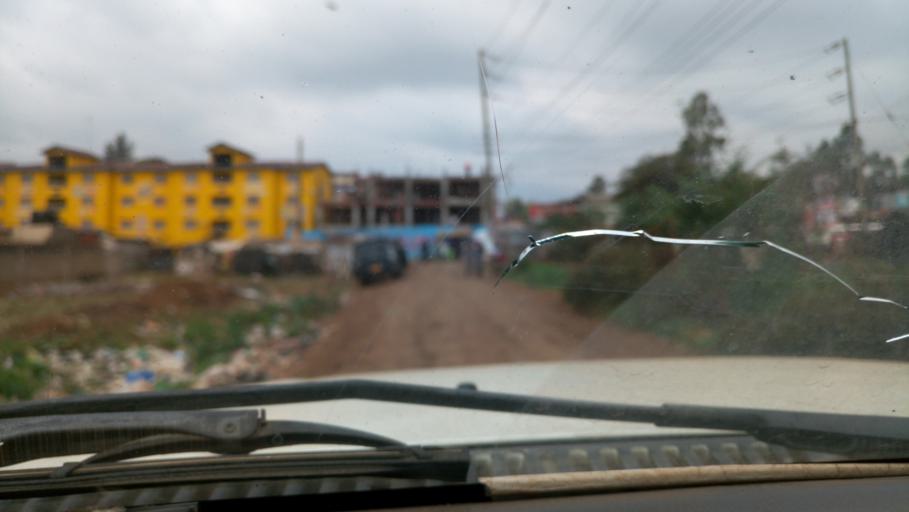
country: KE
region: Kiambu
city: Kikuyu
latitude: -1.2805
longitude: 36.7283
